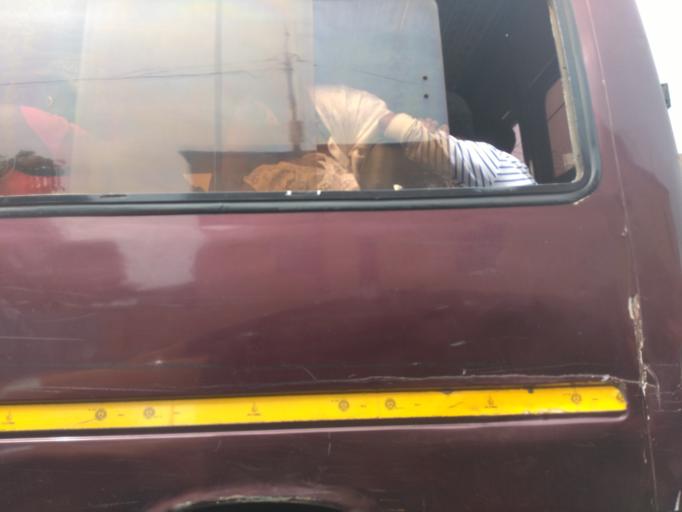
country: GH
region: Greater Accra
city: Accra
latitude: 5.5407
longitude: -0.2153
